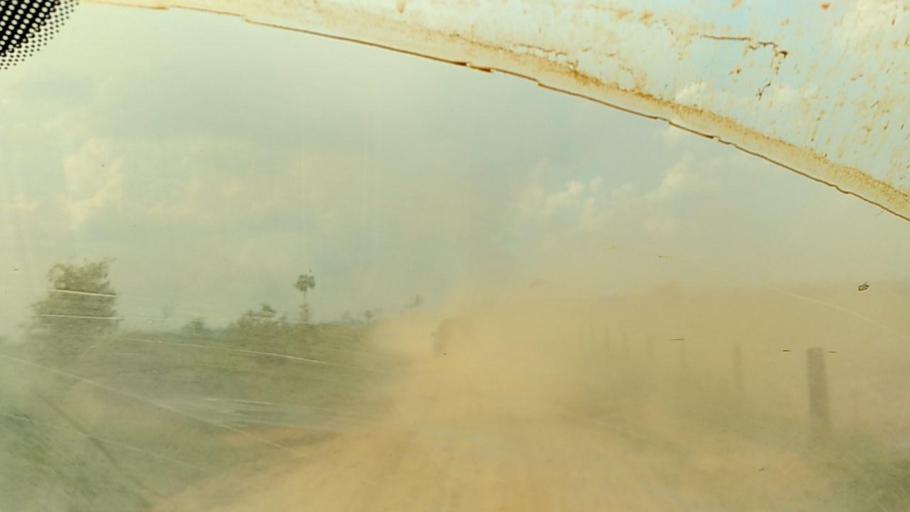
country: BR
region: Rondonia
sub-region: Porto Velho
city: Porto Velho
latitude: -8.6899
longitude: -63.2394
